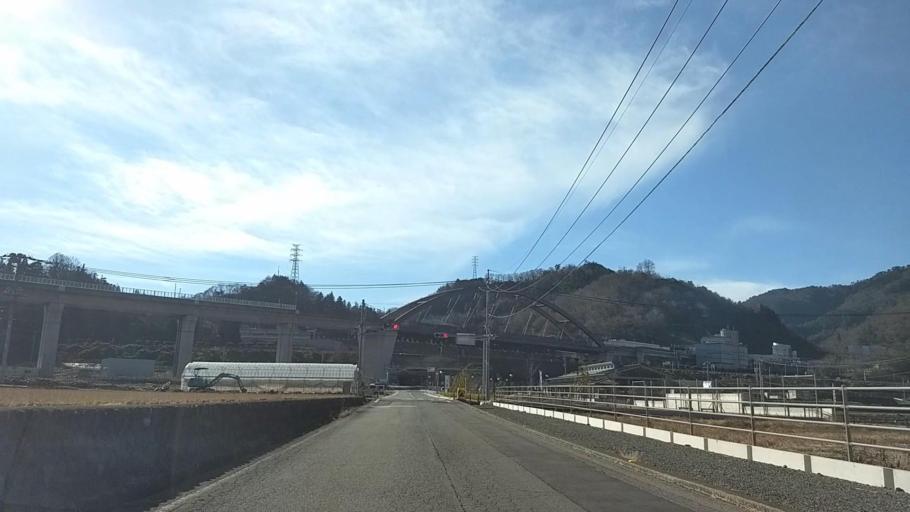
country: JP
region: Yamanashi
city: Otsuki
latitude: 35.5834
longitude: 138.9328
